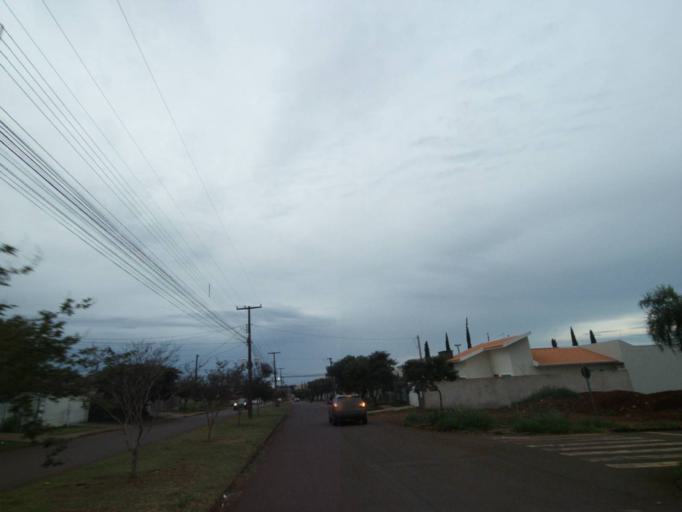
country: BR
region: Parana
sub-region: Campo Mourao
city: Campo Mourao
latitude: -24.0346
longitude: -52.3615
